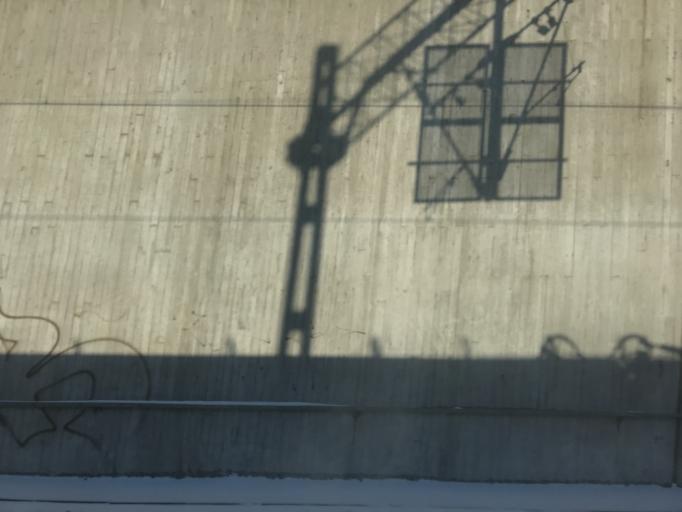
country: SE
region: Skane
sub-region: Burlovs Kommun
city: Arloev
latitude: 55.6277
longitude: 13.0583
